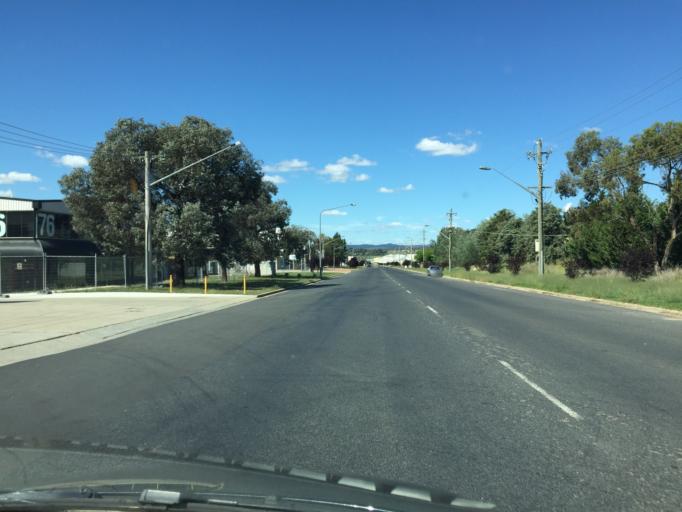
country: AU
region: Australian Capital Territory
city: Macarthur
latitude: -35.3921
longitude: 149.1655
